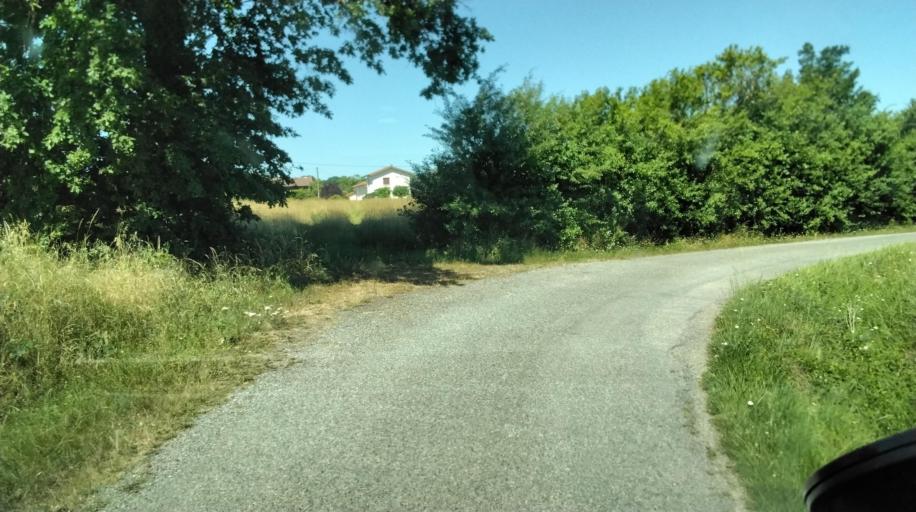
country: FR
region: Midi-Pyrenees
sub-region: Departement de la Haute-Garonne
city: Sainte-Foy-de-Peyrolieres
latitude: 43.4845
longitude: 1.1345
